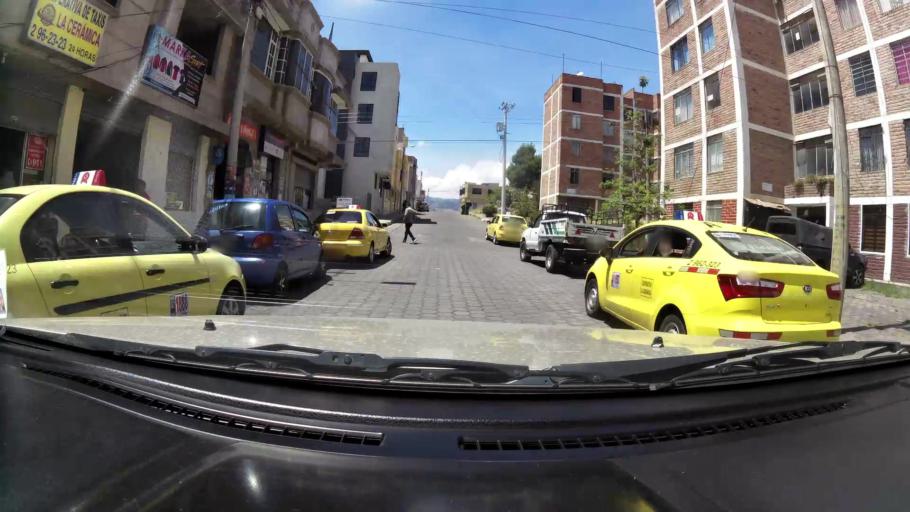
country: EC
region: Chimborazo
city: Riobamba
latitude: -1.6586
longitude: -78.6591
